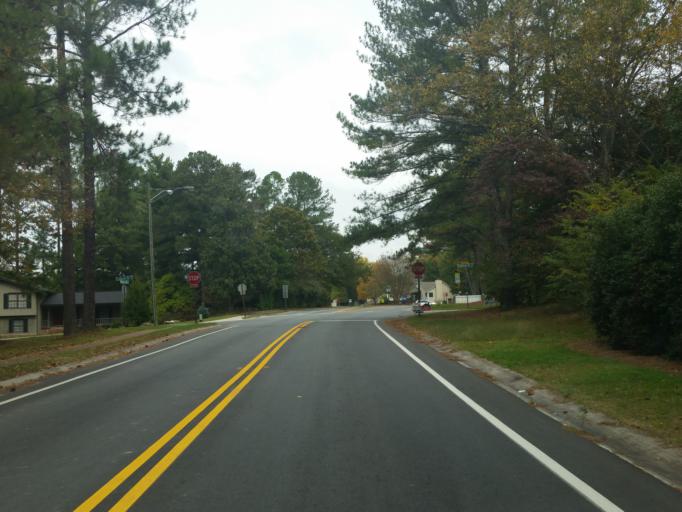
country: US
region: Georgia
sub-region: Fulton County
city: Sandy Springs
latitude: 33.9742
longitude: -84.4379
